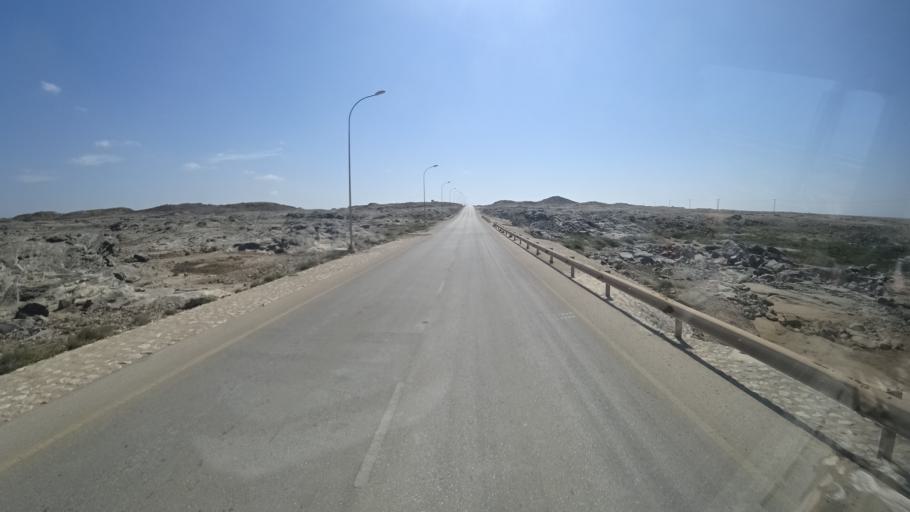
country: OM
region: Zufar
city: Salalah
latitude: 16.9712
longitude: 54.7224
